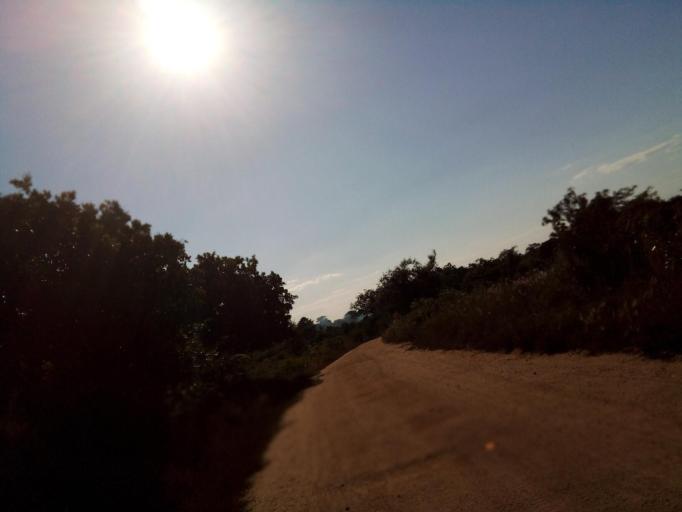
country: MZ
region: Zambezia
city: Quelimane
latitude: -17.4950
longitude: 36.5707
